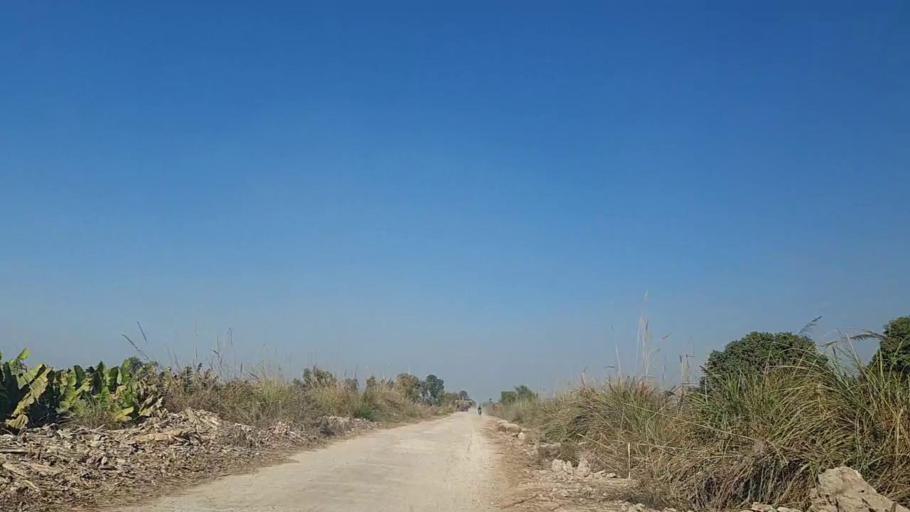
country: PK
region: Sindh
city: Sakrand
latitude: 26.2458
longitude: 68.2206
